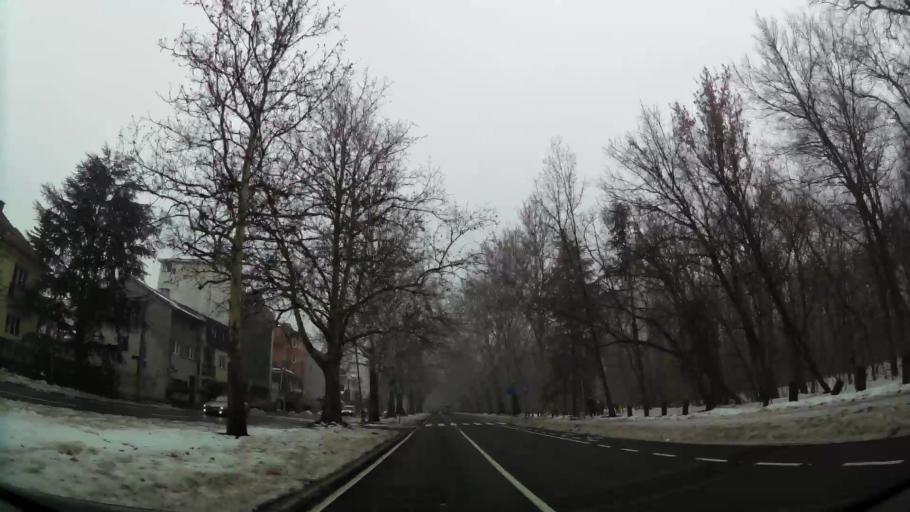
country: RS
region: Central Serbia
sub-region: Belgrade
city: Vozdovac
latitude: 44.7651
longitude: 20.4781
